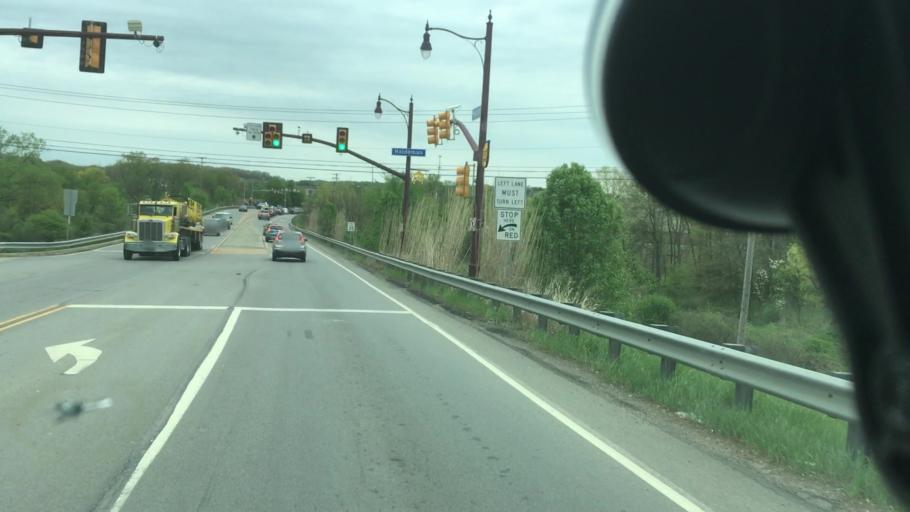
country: US
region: Pennsylvania
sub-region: Butler County
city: Cranberry Township
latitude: 40.6830
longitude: -80.1141
